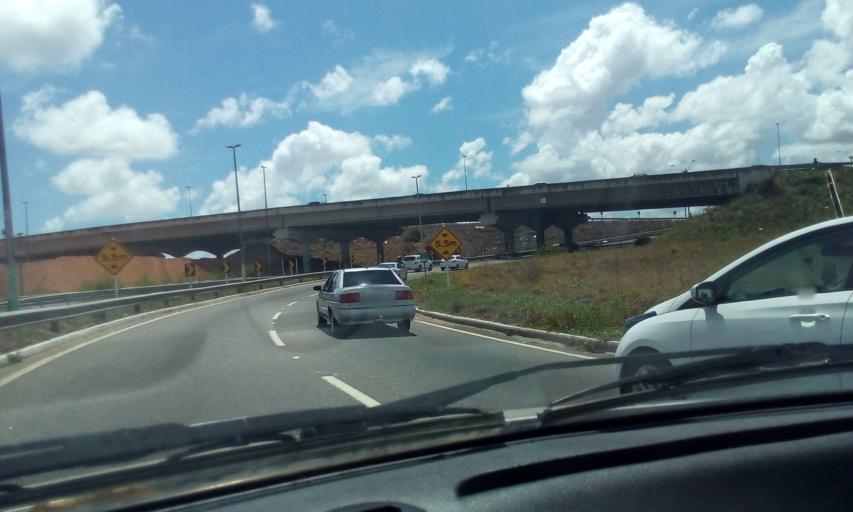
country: BR
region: Rio Grande do Norte
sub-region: Parnamirim
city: Parnamirim
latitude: -5.8913
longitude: -35.2575
